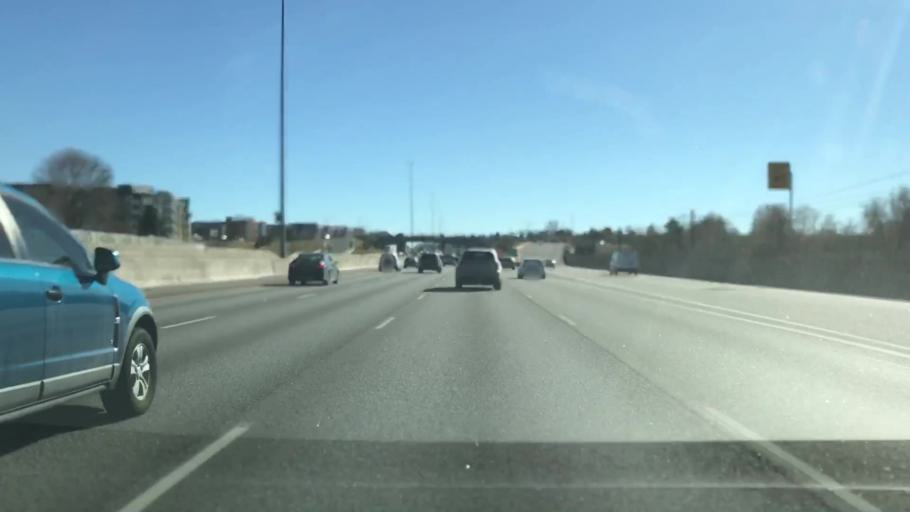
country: US
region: Colorado
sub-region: Arapahoe County
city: Cherry Hills Village
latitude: 39.6567
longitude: -104.9208
